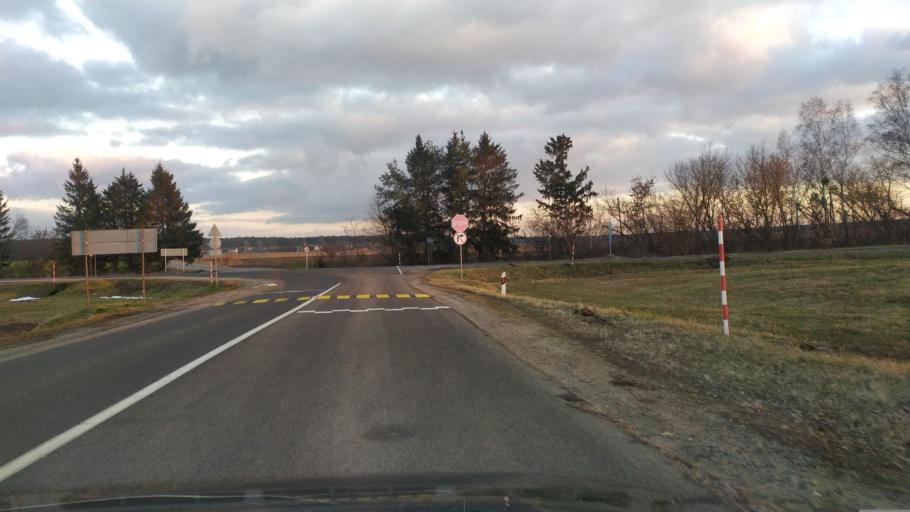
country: BY
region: Brest
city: Kamyanyets
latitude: 52.3707
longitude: 23.7924
